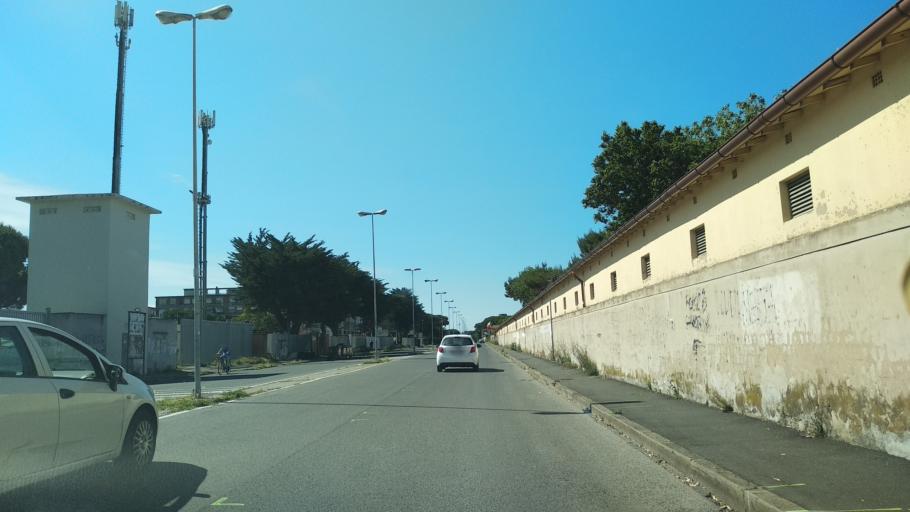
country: IT
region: Tuscany
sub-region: Provincia di Livorno
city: Livorno
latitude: 43.5250
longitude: 10.3157
